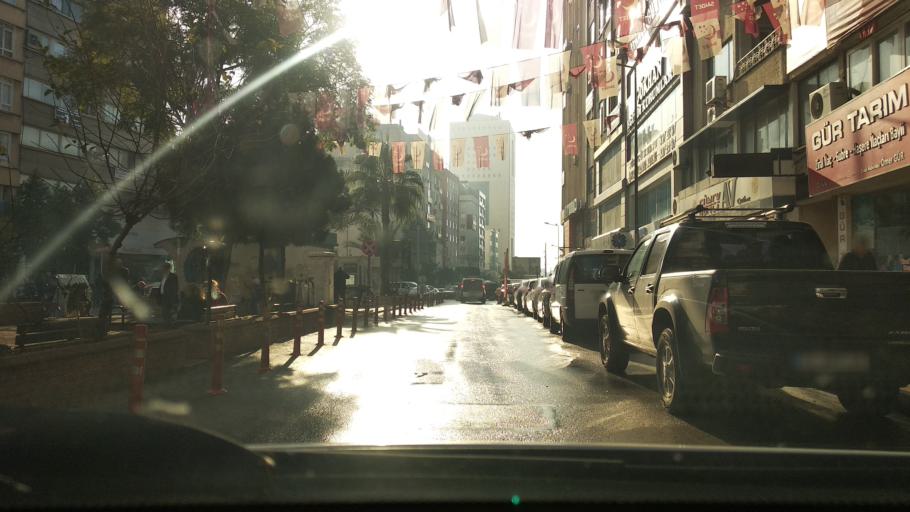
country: TR
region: Mersin
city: Mercin
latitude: 36.8054
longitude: 34.6229
